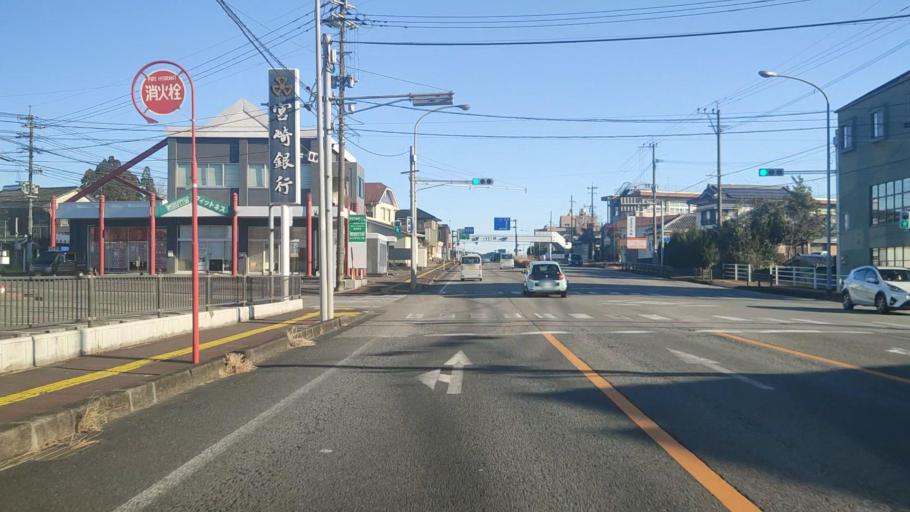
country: JP
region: Miyazaki
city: Nobeoka
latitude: 32.4711
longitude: 131.6506
